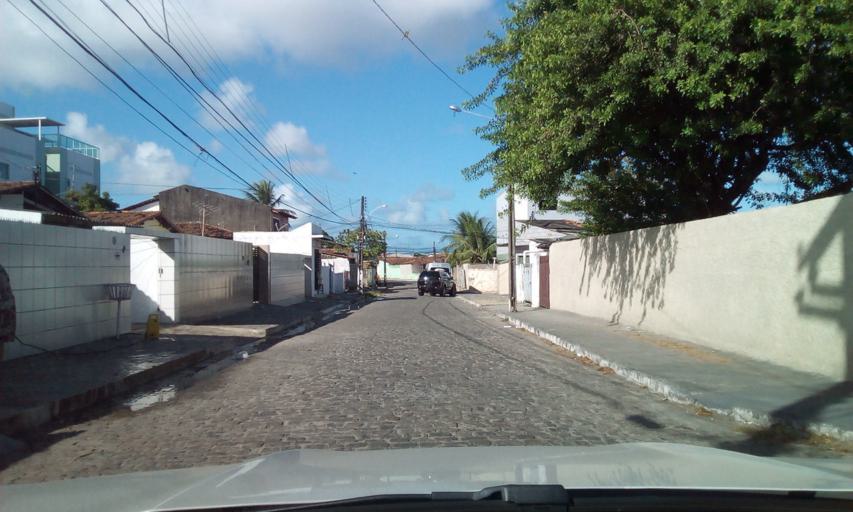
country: BR
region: Paraiba
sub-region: Joao Pessoa
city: Joao Pessoa
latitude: -7.1732
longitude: -34.8386
